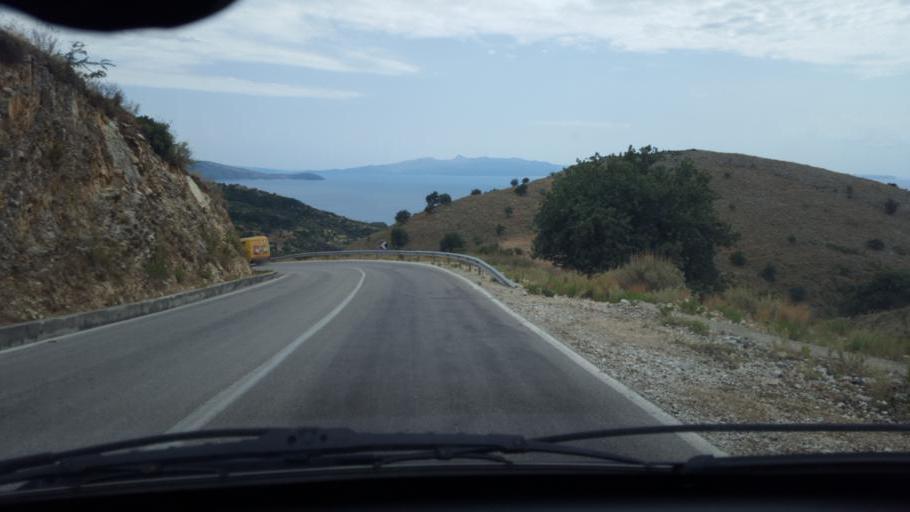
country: AL
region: Vlore
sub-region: Rrethi i Sarandes
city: Lukove
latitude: 40.0406
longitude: 19.8776
